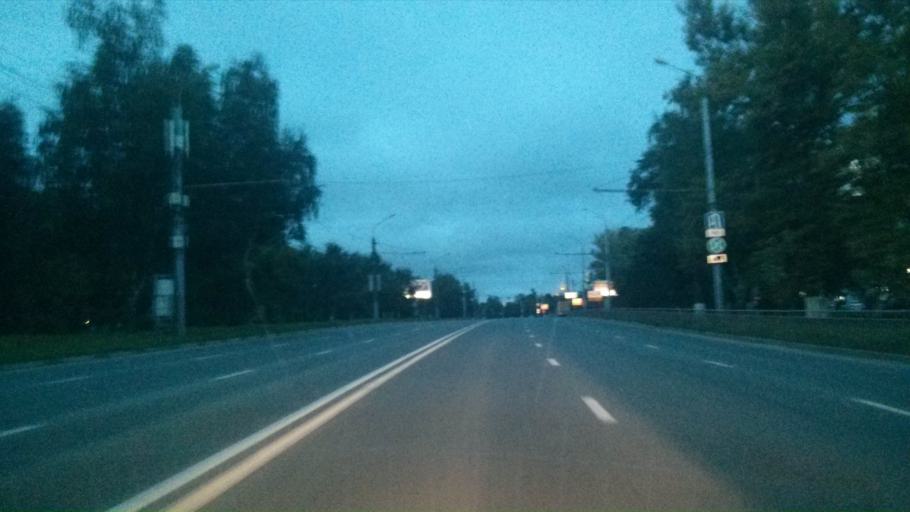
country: RU
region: Nizjnij Novgorod
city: Nizhniy Novgorod
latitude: 56.2330
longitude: 43.9496
